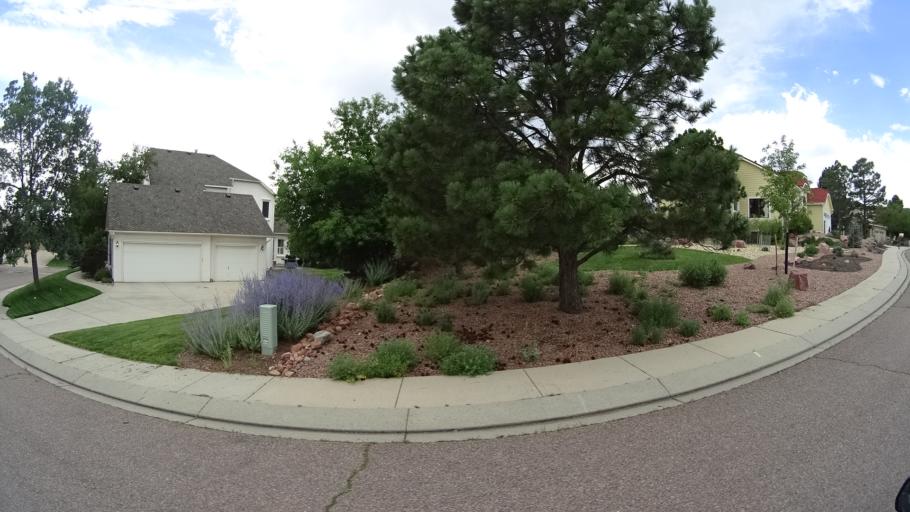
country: US
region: Colorado
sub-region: El Paso County
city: Colorado Springs
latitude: 38.9098
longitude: -104.8363
